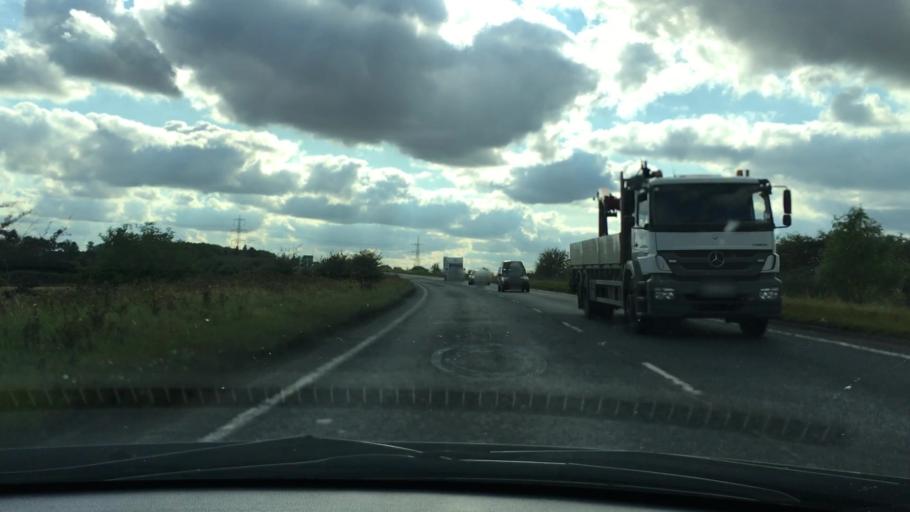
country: GB
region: England
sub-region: North East Lincolnshire
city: Immingham
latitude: 53.6014
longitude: -0.1931
